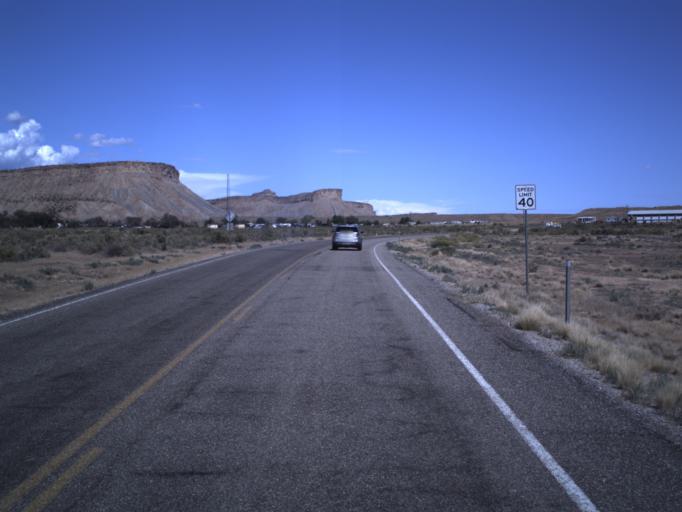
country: US
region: Utah
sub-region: Grand County
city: Moab
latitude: 38.9646
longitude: -109.7223
